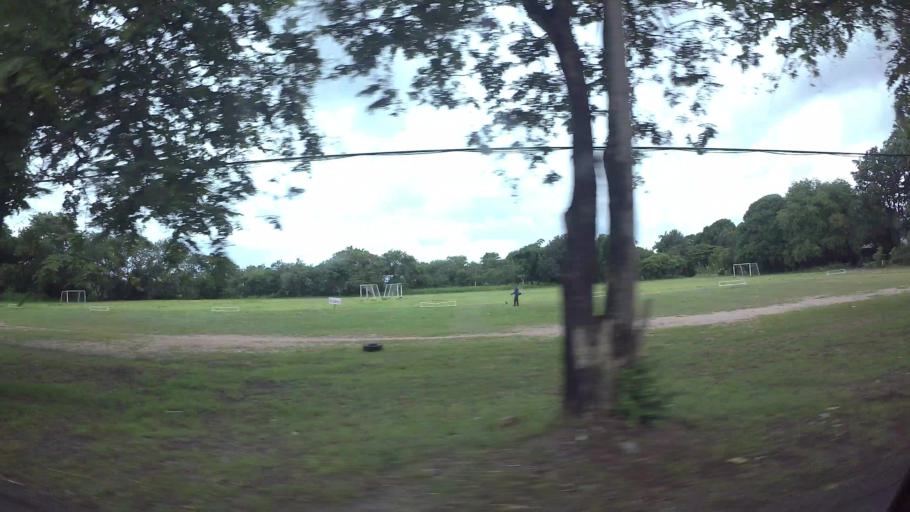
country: TH
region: Chon Buri
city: Si Racha
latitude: 13.2138
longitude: 100.9622
